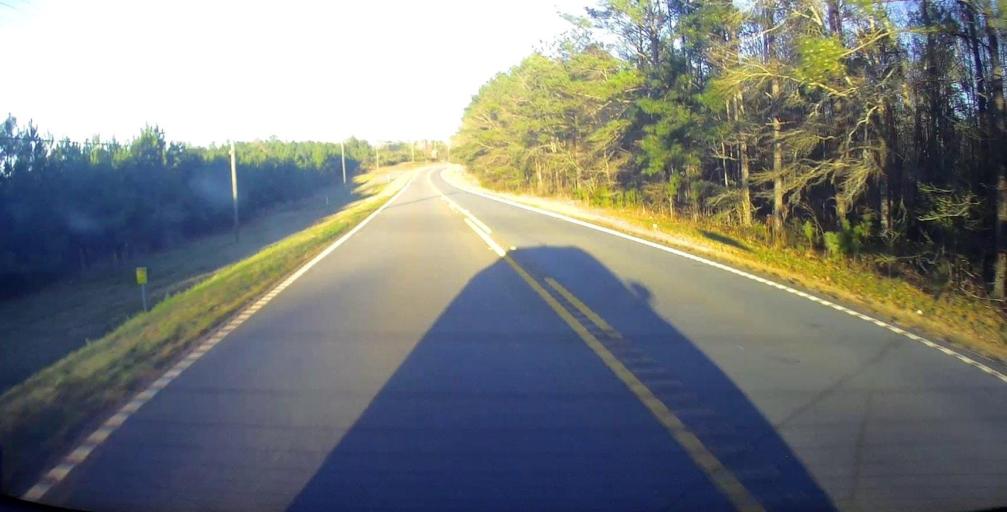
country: US
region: Georgia
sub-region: Harris County
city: Hamilton
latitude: 32.6726
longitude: -84.9438
